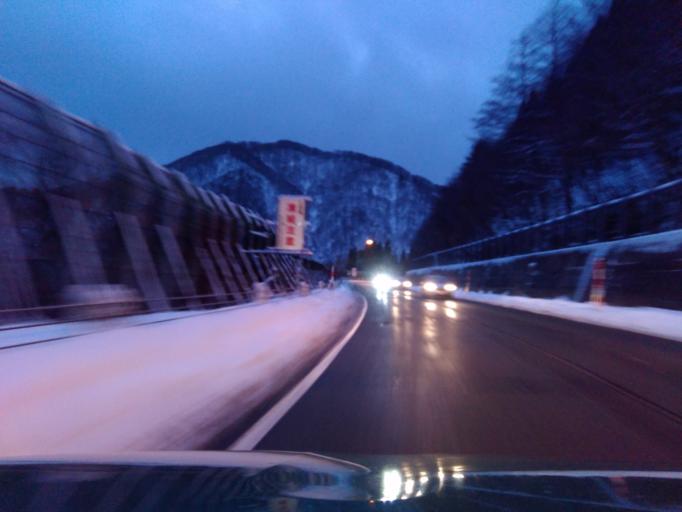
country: JP
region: Iwate
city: Shizukuishi
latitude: 39.6895
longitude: 140.7952
